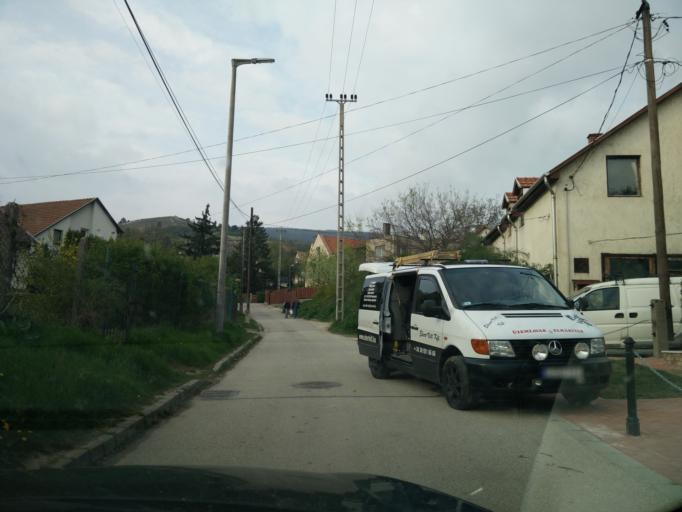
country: HU
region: Pest
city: Budaors
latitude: 47.4656
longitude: 18.9528
